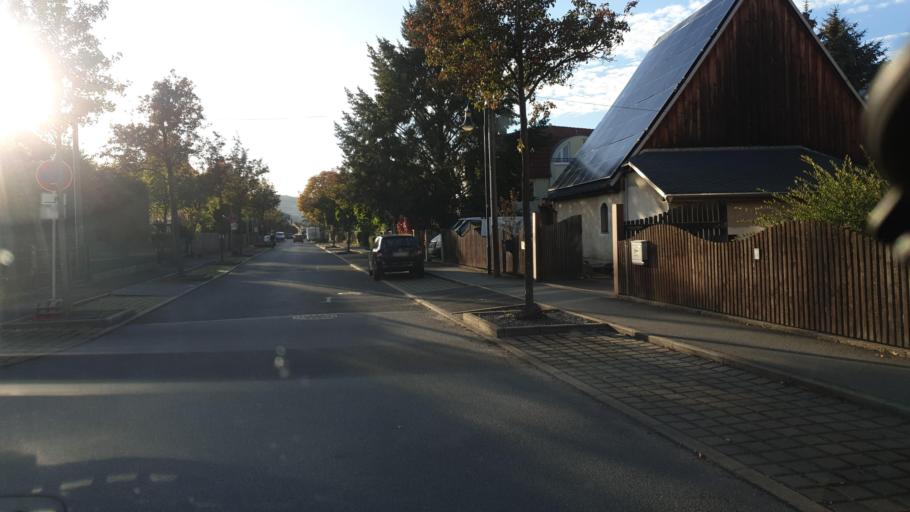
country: DE
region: Saxony
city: Radebeul
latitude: 51.0891
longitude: 13.6374
